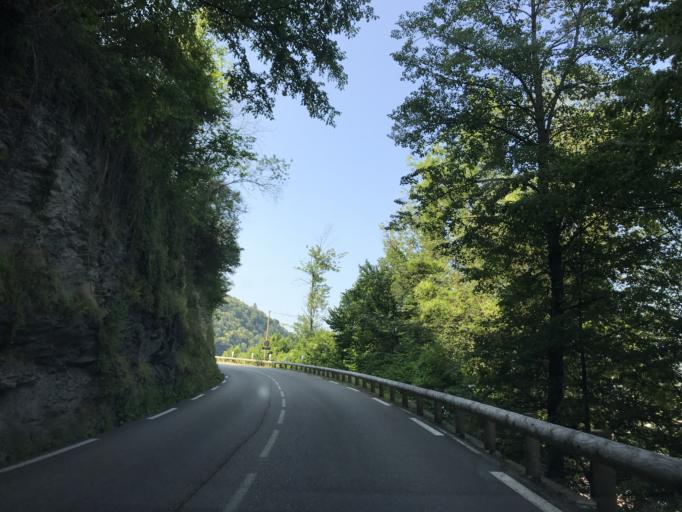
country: FR
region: Rhone-Alpes
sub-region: Departement de l'Isere
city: Allevard
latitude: 45.3954
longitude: 6.0795
